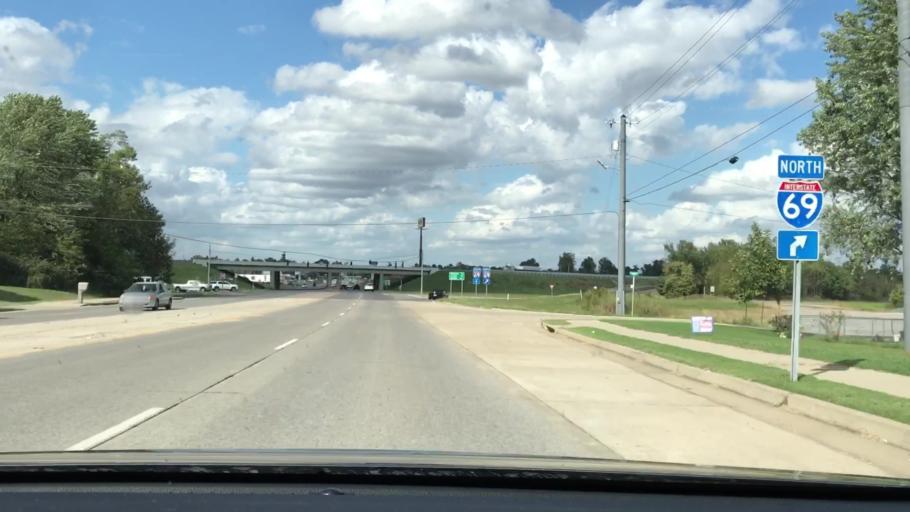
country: US
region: Kentucky
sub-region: Graves County
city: Mayfield
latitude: 36.7650
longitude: -88.6427
